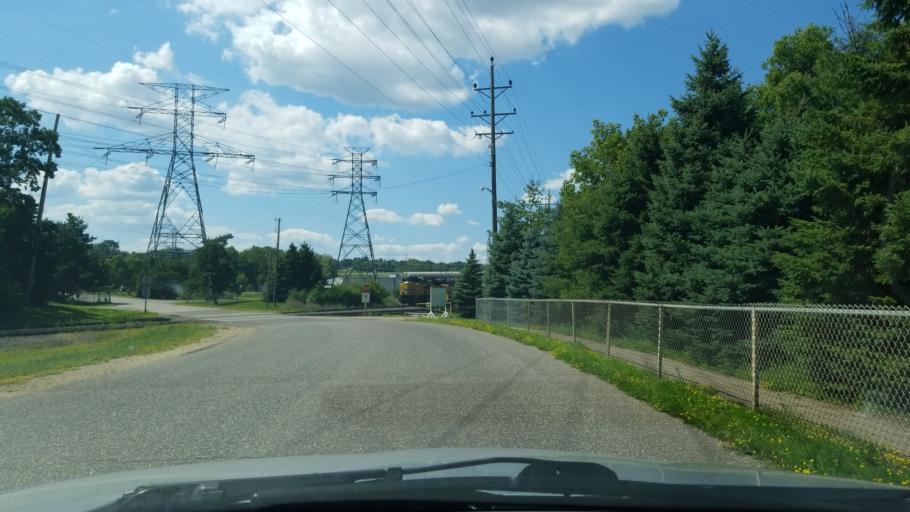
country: US
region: Minnesota
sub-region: Washington County
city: Oak Park Heights
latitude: 45.0317
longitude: -92.7858
